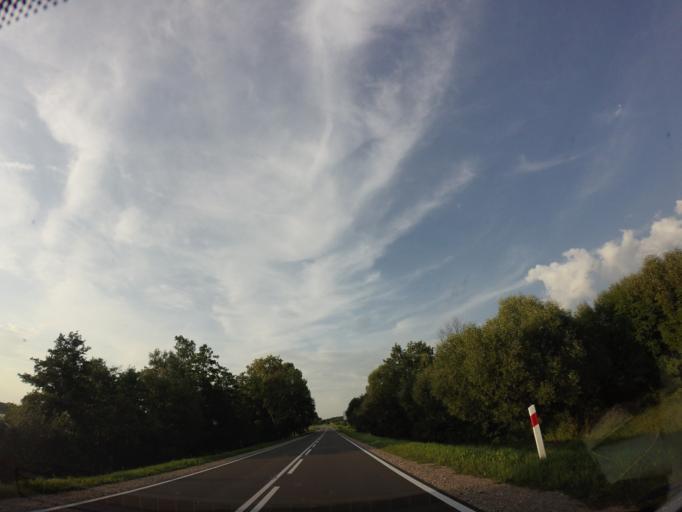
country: LT
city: Lazdijai
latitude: 54.1350
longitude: 23.4644
